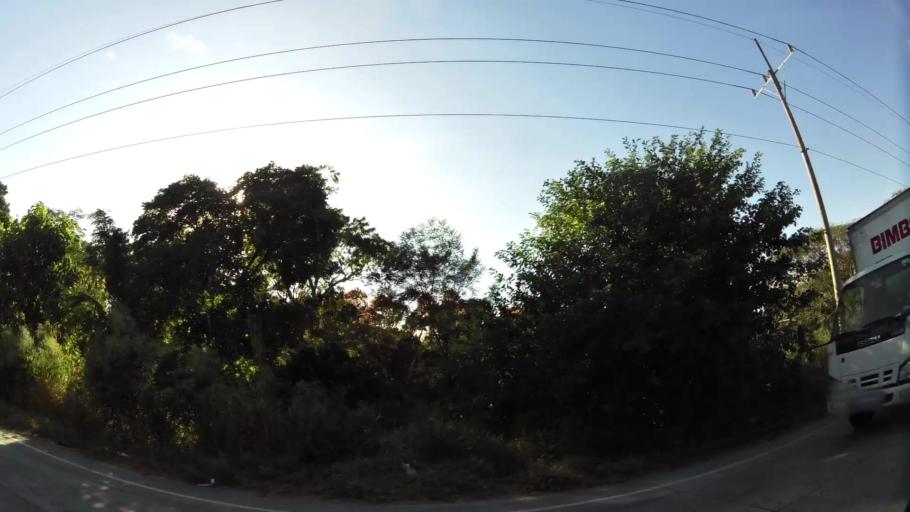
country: SV
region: Santa Ana
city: Metapan
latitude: 14.2768
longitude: -89.4610
